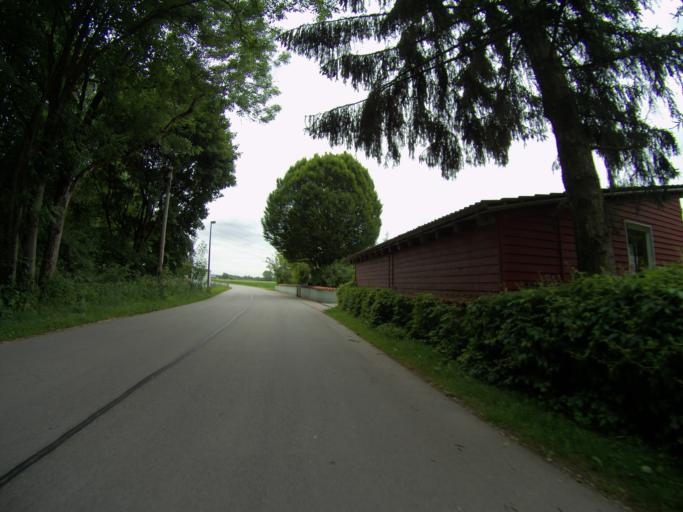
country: DE
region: Bavaria
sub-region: Upper Bavaria
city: Langenbach
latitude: 48.4068
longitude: 11.8651
